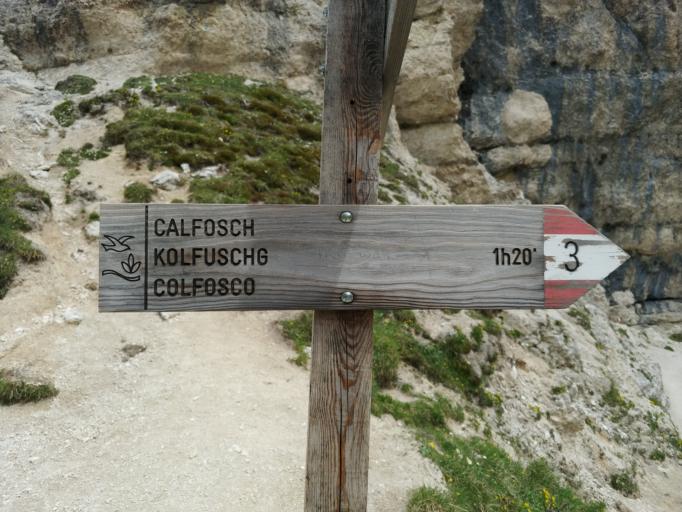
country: IT
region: Trentino-Alto Adige
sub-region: Bolzano
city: Corvara in Badia
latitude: 46.5771
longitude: 11.8376
